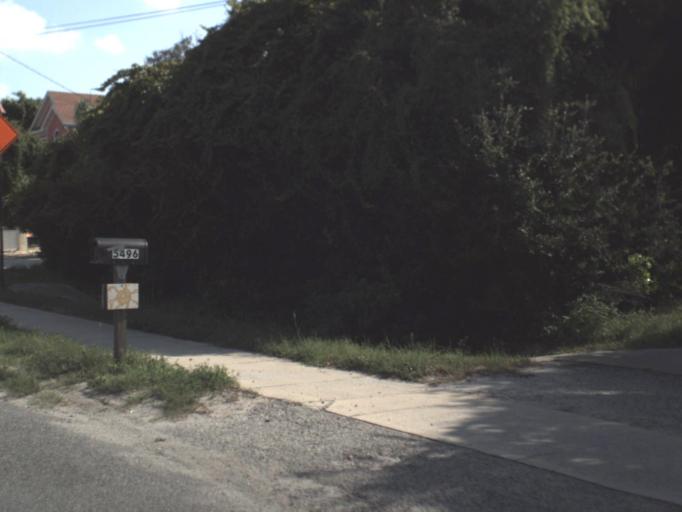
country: US
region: Florida
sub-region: Saint Johns County
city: Butler Beach
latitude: 29.7925
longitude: -81.2614
